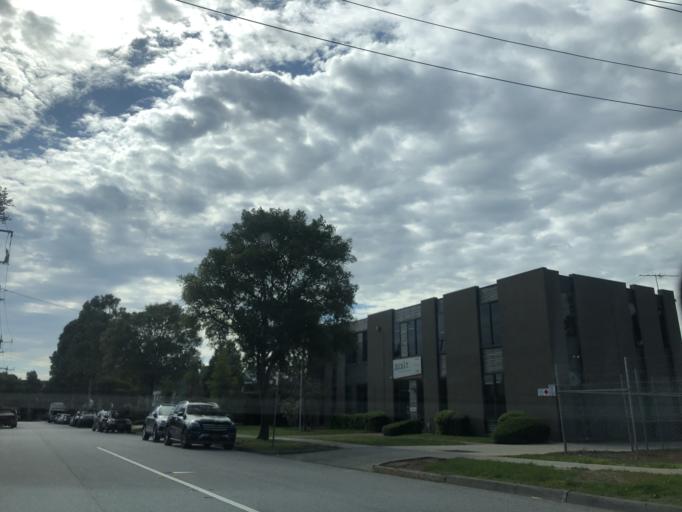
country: AU
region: Victoria
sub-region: Monash
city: Notting Hill
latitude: -37.9071
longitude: 145.1561
